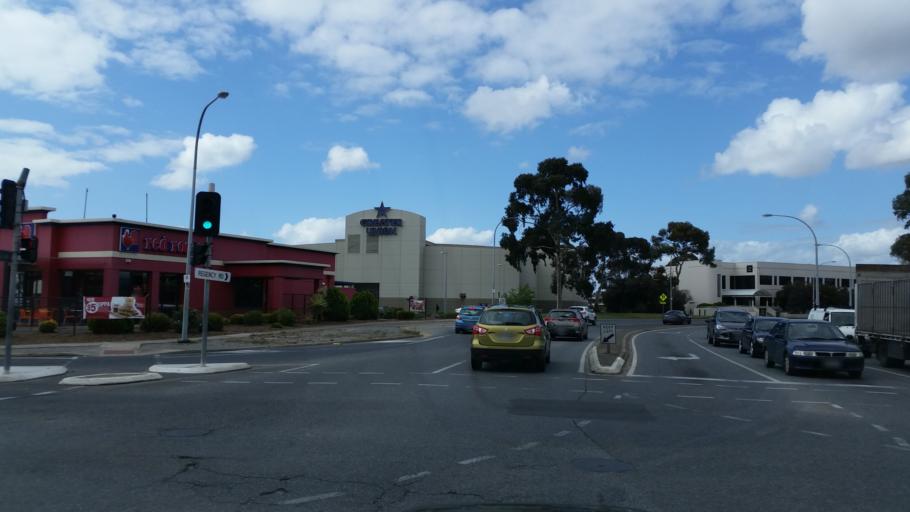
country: AU
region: South Australia
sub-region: Charles Sturt
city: Woodville
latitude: -34.8768
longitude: 138.5508
